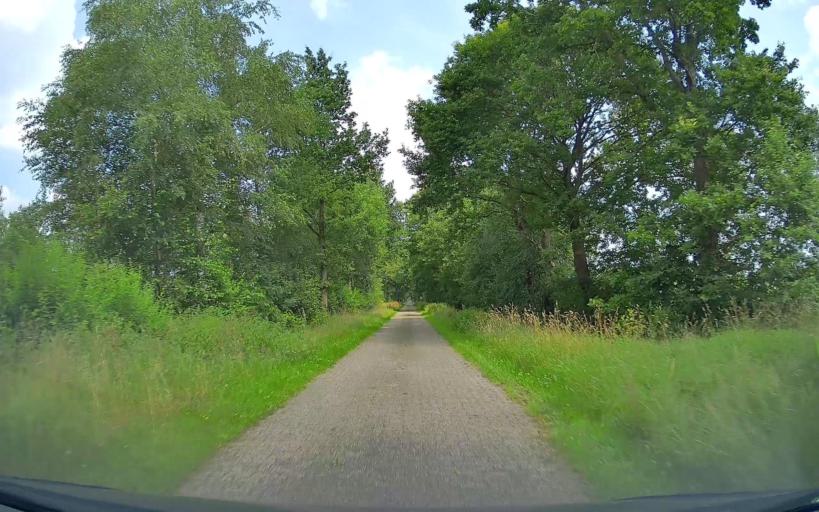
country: DE
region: Lower Saxony
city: Bosel
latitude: 52.9998
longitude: 7.9032
